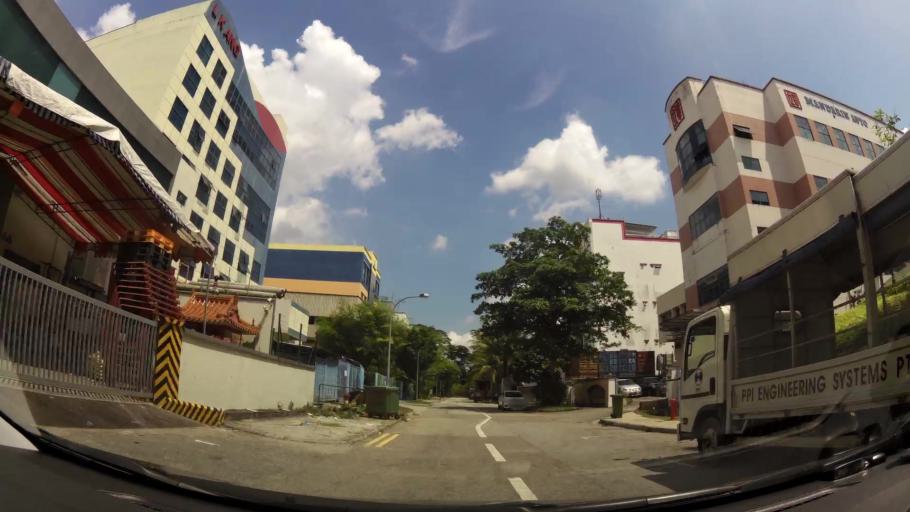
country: MY
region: Johor
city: Kampung Pasir Gudang Baru
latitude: 1.3879
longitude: 103.8286
